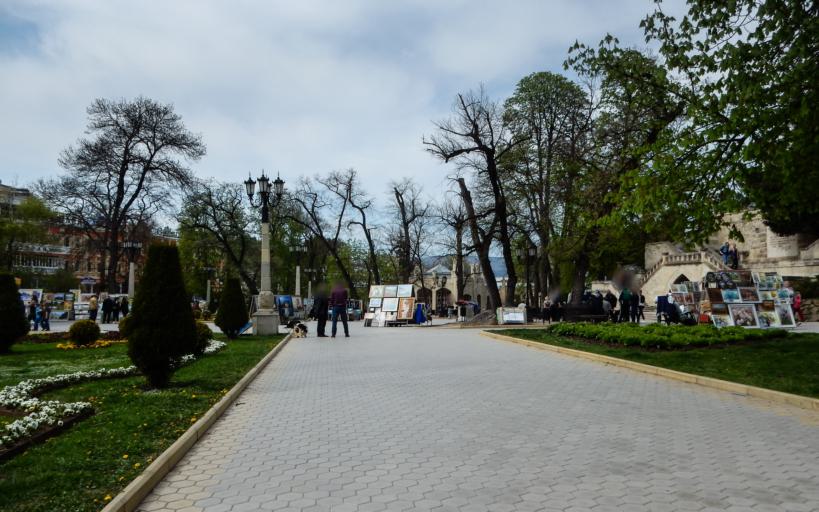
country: RU
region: Stavropol'skiy
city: Kislovodsk
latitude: 43.8986
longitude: 42.7174
